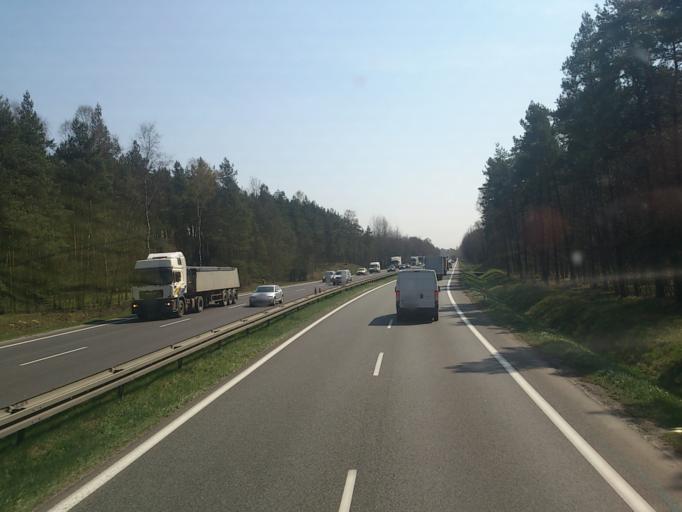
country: PL
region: Silesian Voivodeship
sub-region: Powiat bedzinski
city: Siewierz
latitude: 50.5268
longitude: 19.1920
